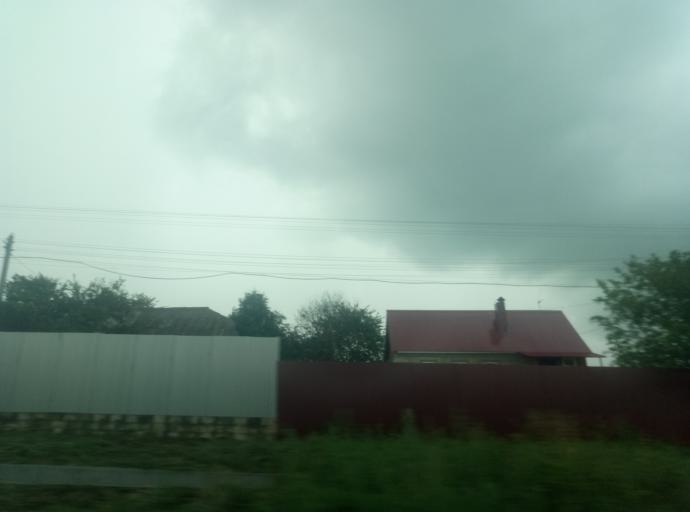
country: RU
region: Tula
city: Kireyevsk
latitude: 53.9897
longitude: 37.9291
